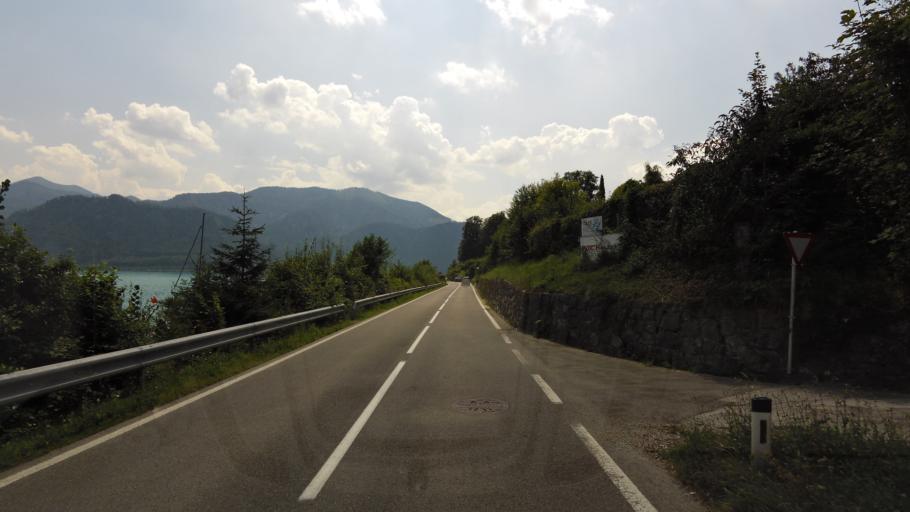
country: AT
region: Upper Austria
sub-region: Politischer Bezirk Vocklabruck
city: Steinbach am Attersee
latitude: 47.8183
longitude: 13.5080
